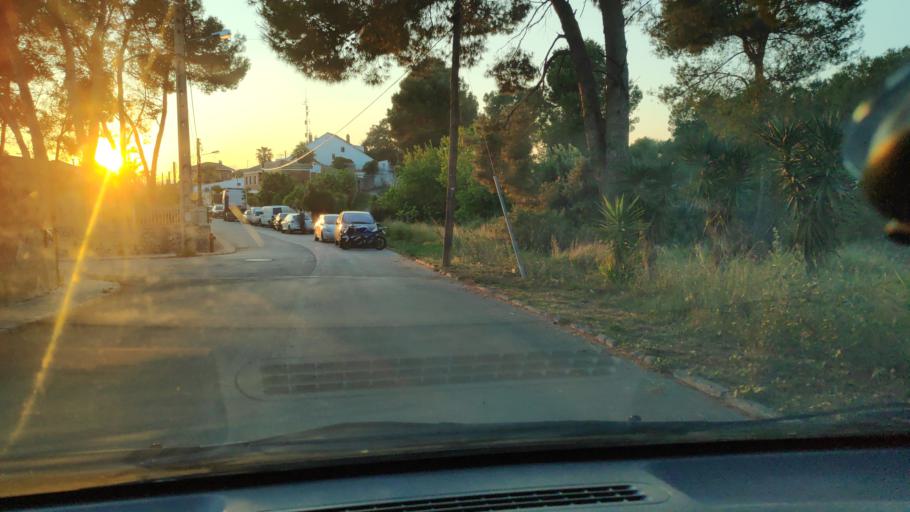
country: ES
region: Catalonia
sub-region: Provincia de Barcelona
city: Sant Quirze del Valles
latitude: 41.5316
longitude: 2.0515
